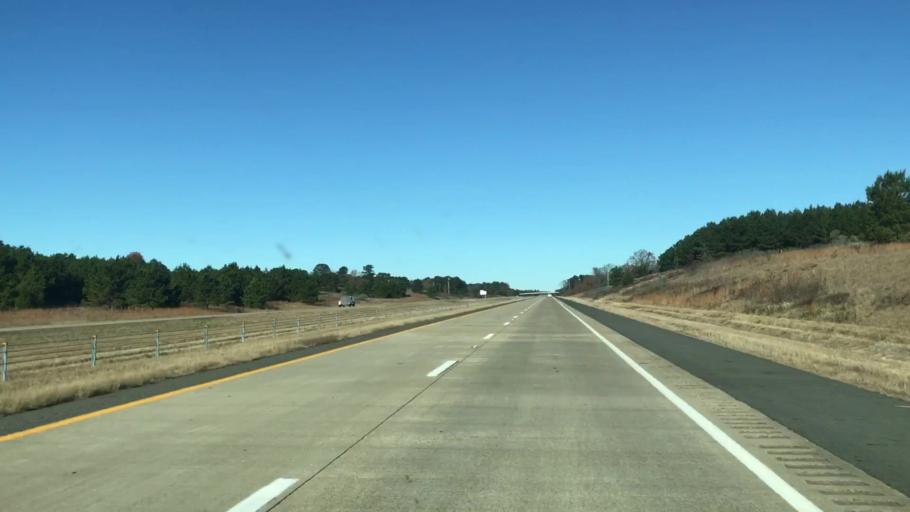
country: US
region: Texas
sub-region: Bowie County
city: Texarkana
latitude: 33.2805
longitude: -93.9087
